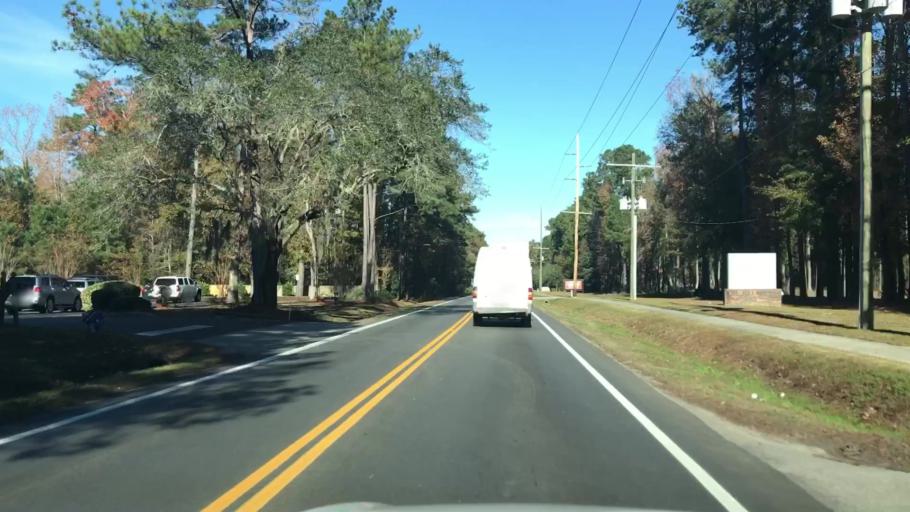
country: US
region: South Carolina
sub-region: Dorchester County
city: Summerville
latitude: 32.9995
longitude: -80.2304
